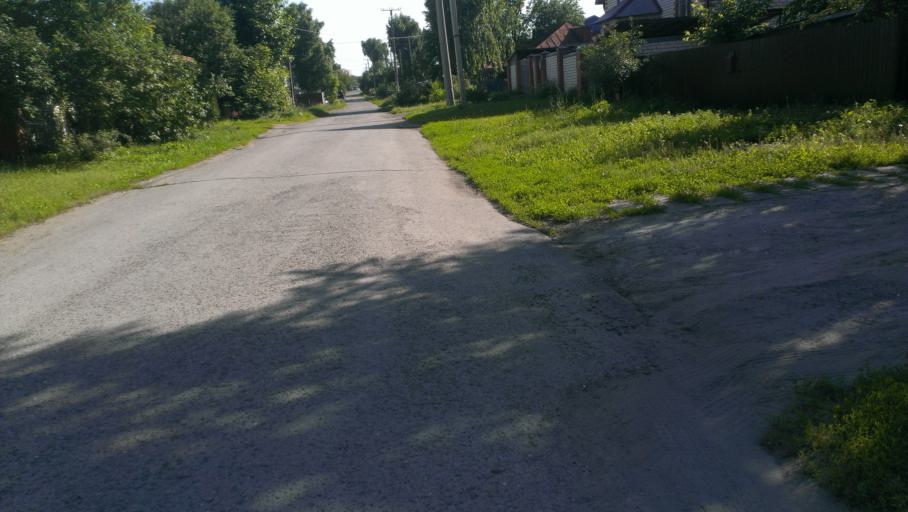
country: RU
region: Altai Krai
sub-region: Gorod Barnaulskiy
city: Barnaul
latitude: 53.3571
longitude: 83.7411
